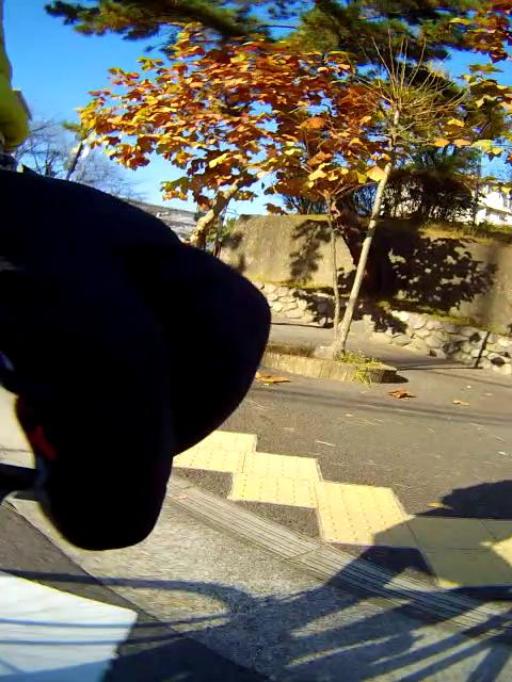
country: JP
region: Hyogo
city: Takarazuka
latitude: 34.7892
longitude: 135.3389
